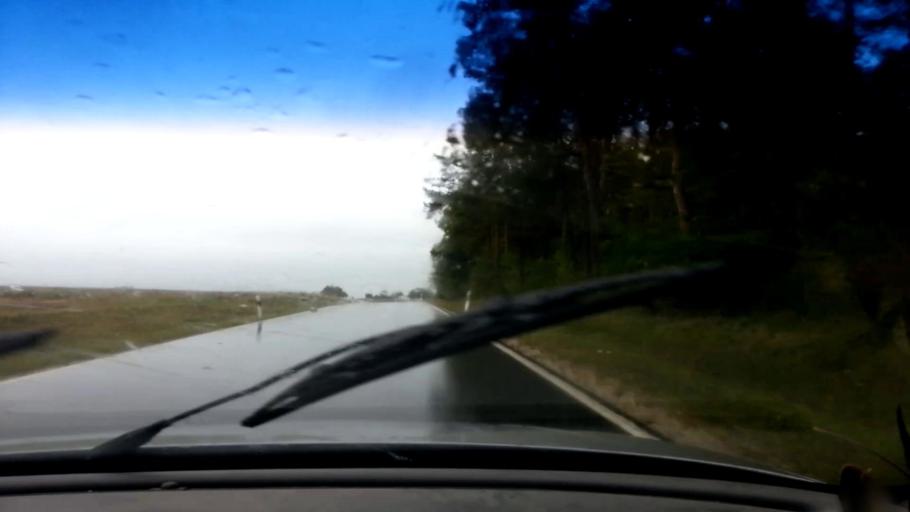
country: DE
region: Bavaria
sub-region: Upper Franconia
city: Heiligenstadt
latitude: 49.9003
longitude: 11.1533
